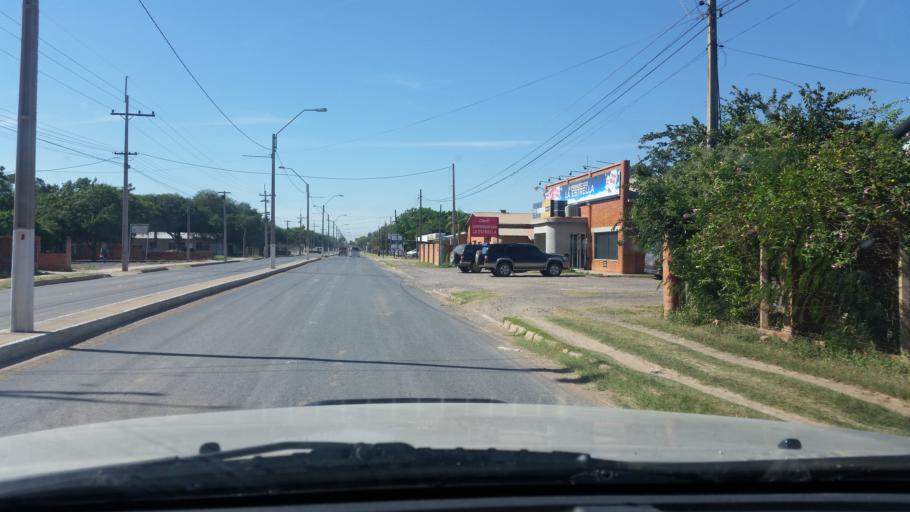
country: PY
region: Boqueron
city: Colonia Menno
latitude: -22.3713
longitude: -59.8374
